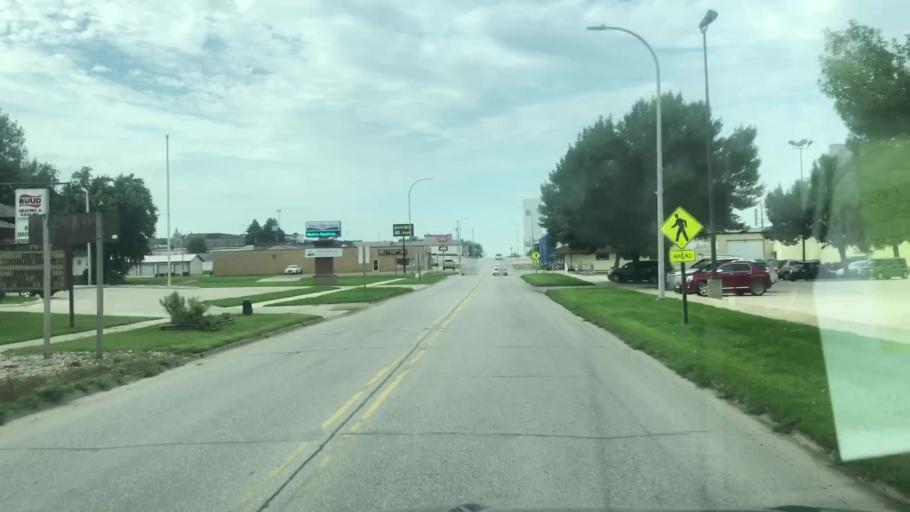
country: US
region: Iowa
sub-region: O'Brien County
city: Sheldon
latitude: 43.1843
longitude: -95.8549
